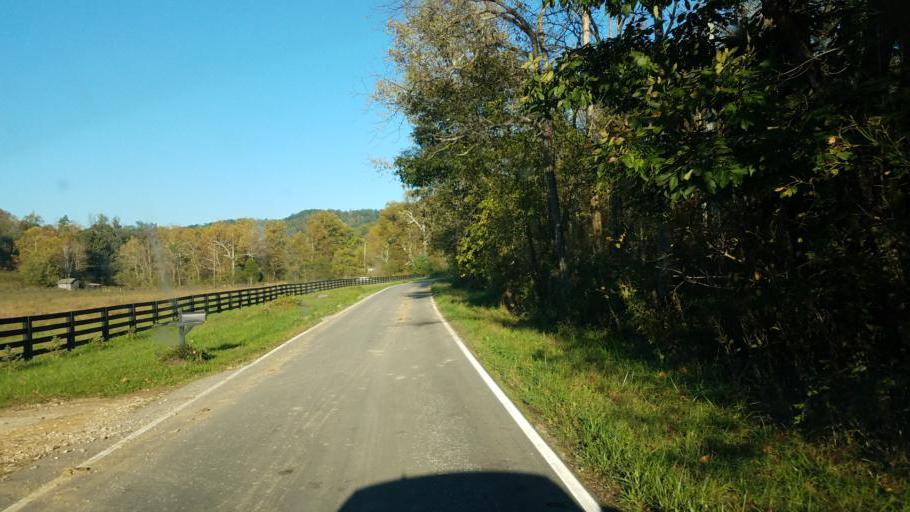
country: US
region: Kentucky
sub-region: Lewis County
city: Vanceburg
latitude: 38.5098
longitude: -83.4890
